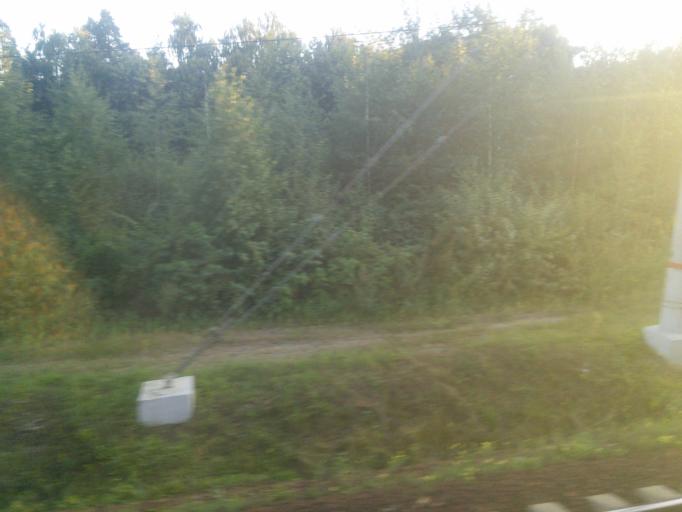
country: RU
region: Moskovskaya
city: Kupavna
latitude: 55.7458
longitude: 38.1477
